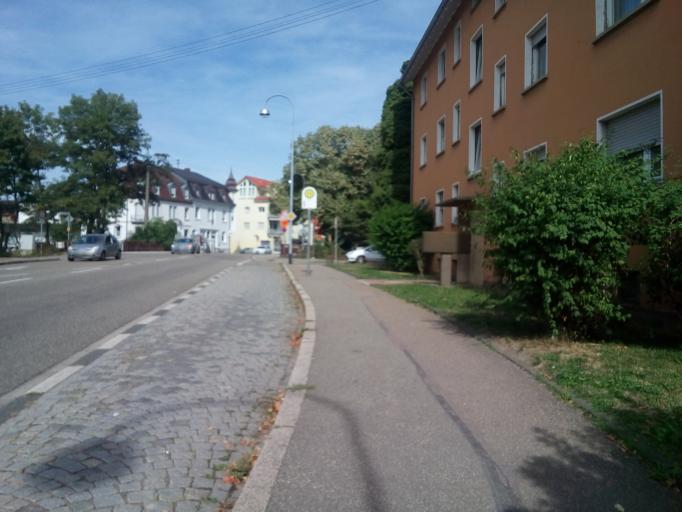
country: DE
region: Baden-Wuerttemberg
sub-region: Karlsruhe Region
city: Sinzheim
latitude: 48.7854
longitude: 8.1918
